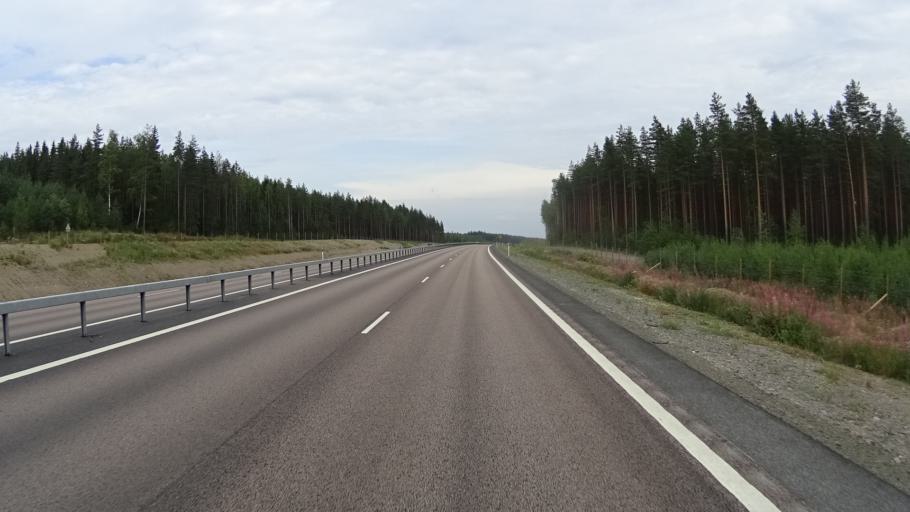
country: FI
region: South Karelia
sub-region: Lappeenranta
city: Lemi
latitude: 61.0029
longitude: 27.9474
